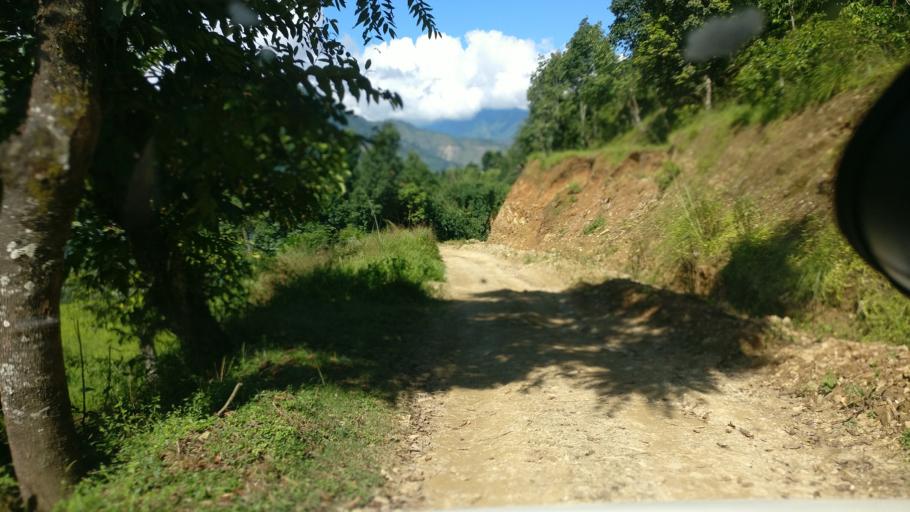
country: NP
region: Western Region
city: Baglung
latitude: 28.1379
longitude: 83.6528
